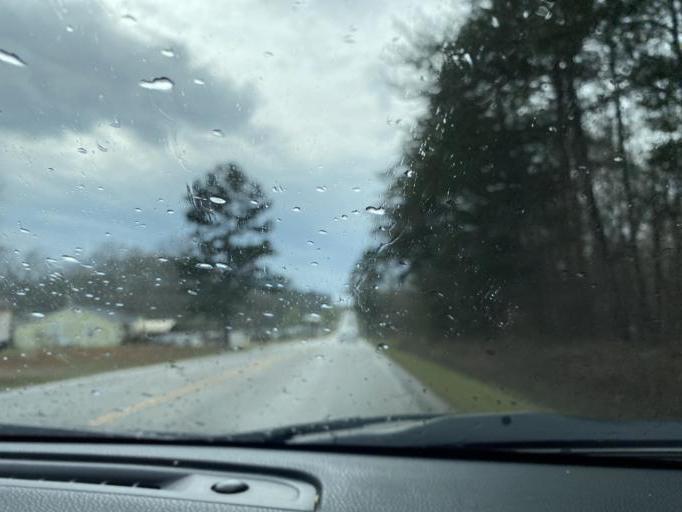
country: US
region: South Carolina
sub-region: Spartanburg County
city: Cowpens
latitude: 35.0171
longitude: -81.7669
